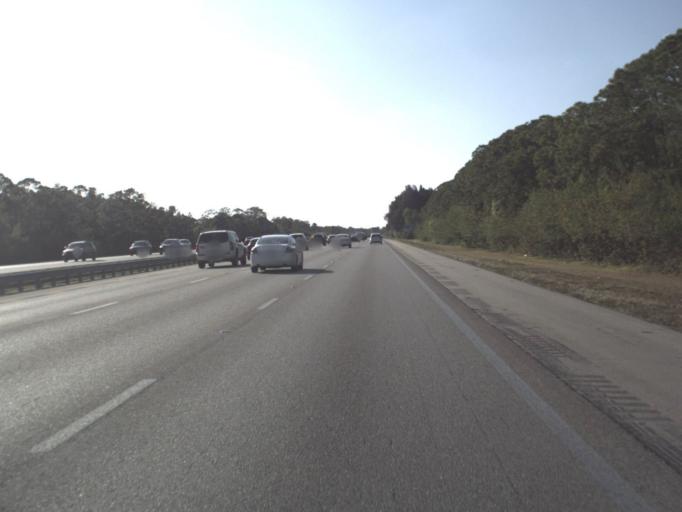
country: US
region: Florida
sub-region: Brevard County
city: June Park
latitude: 28.0595
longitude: -80.6873
